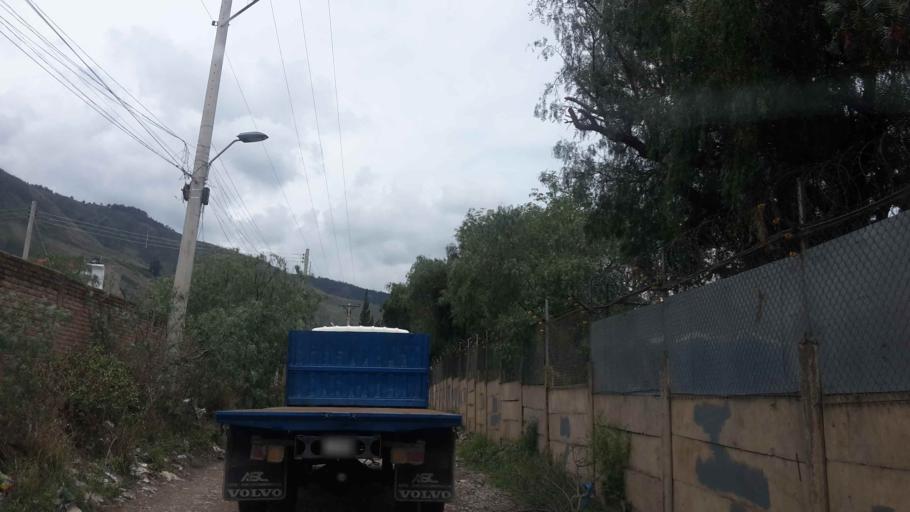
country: BO
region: Cochabamba
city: Cochabamba
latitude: -17.3375
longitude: -66.1865
